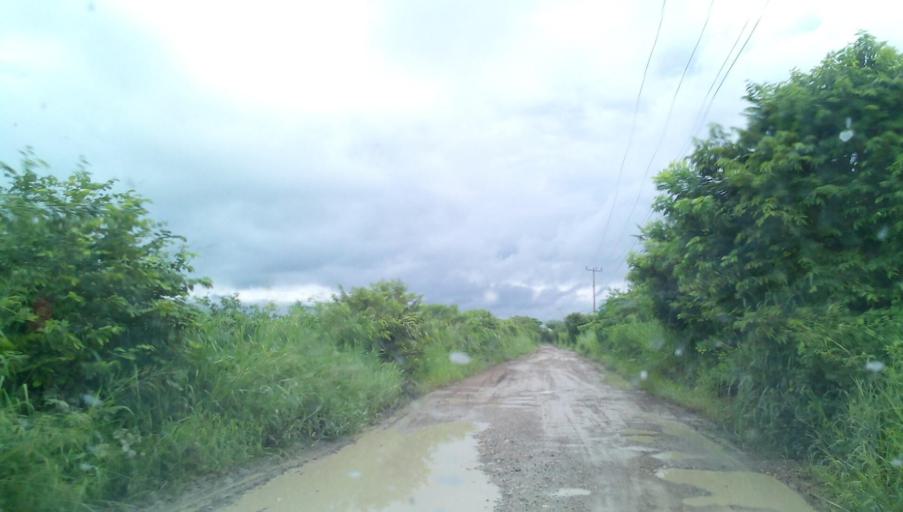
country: MX
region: Veracruz
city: Panuco
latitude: 21.8429
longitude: -98.1357
